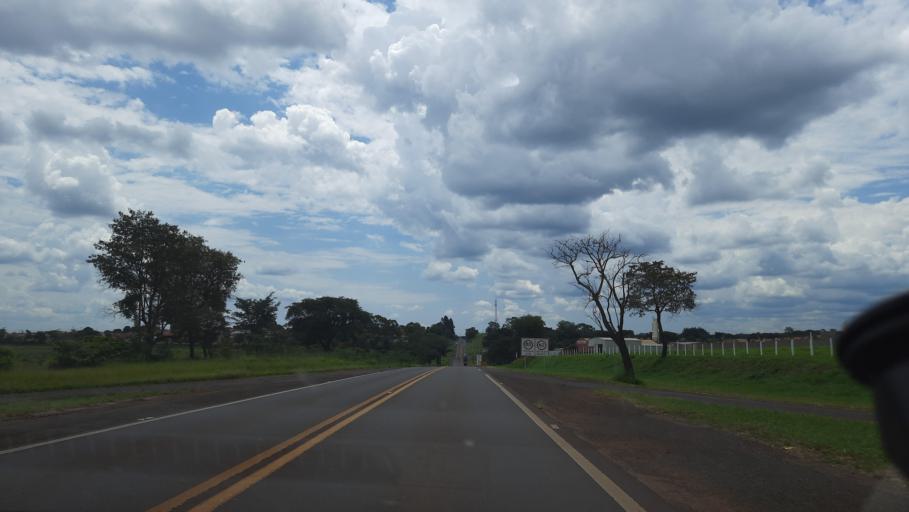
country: BR
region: Sao Paulo
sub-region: Cajuru
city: Cajuru
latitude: -21.2781
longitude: -47.2884
